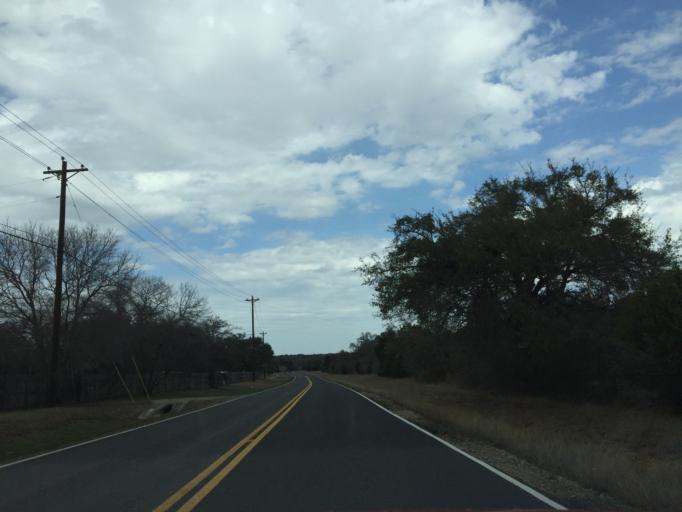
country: US
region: Texas
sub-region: Burnet County
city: Bertram
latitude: 30.7076
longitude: -97.9282
